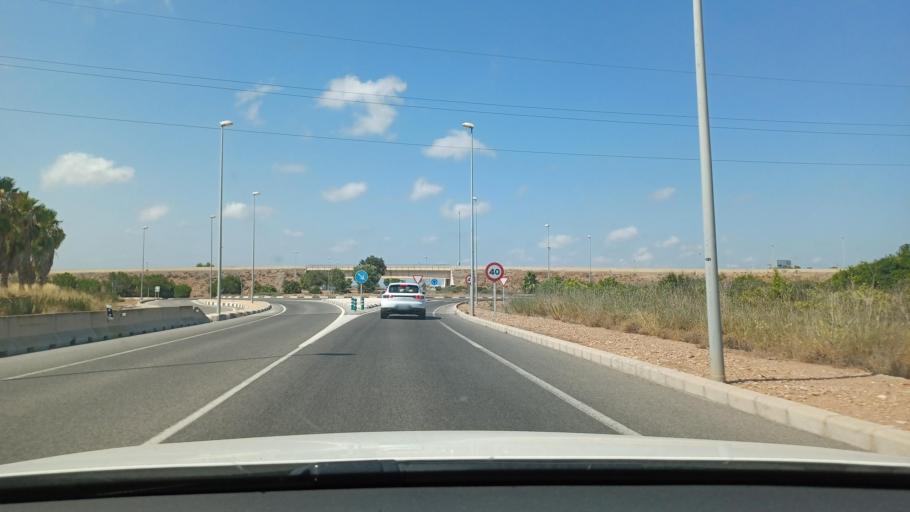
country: ES
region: Valencia
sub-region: Provincia de Castello
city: Moncofar
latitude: 39.8143
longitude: -0.1672
